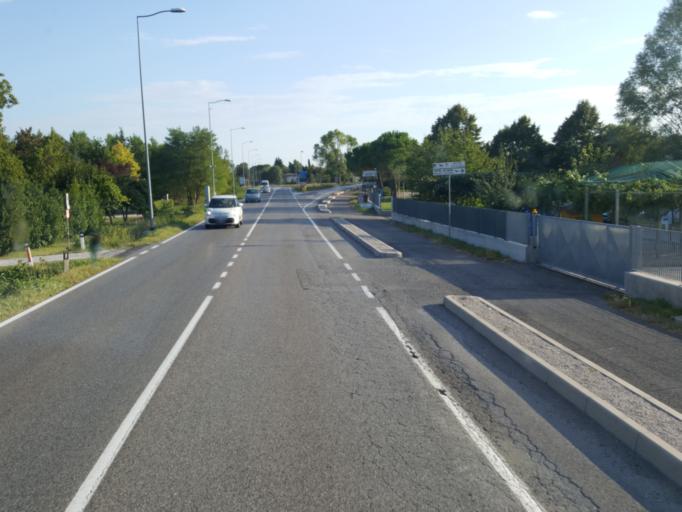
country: IT
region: Friuli Venezia Giulia
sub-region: Provincia di Udine
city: Porpetto
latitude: 45.8444
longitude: 13.2116
